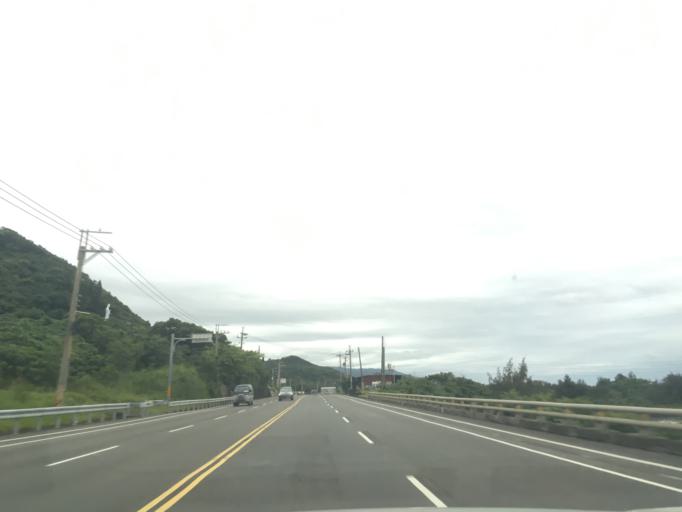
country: TW
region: Taiwan
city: Hengchun
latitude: 22.3001
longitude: 120.8888
